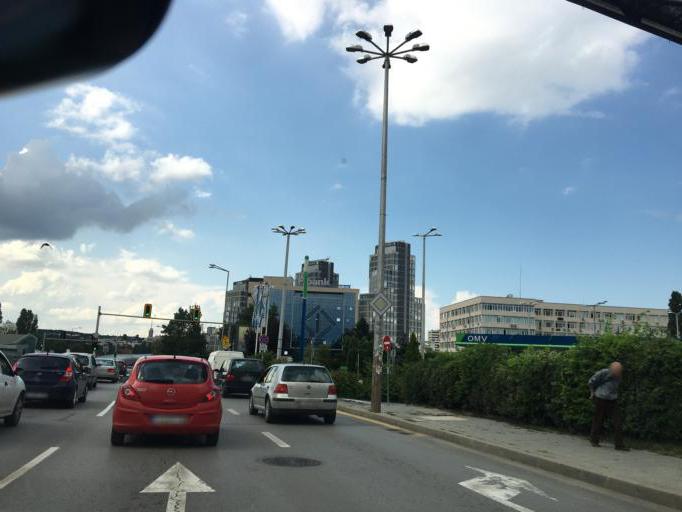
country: BG
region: Sofia-Capital
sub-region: Stolichna Obshtina
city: Sofia
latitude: 42.6627
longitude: 23.3583
